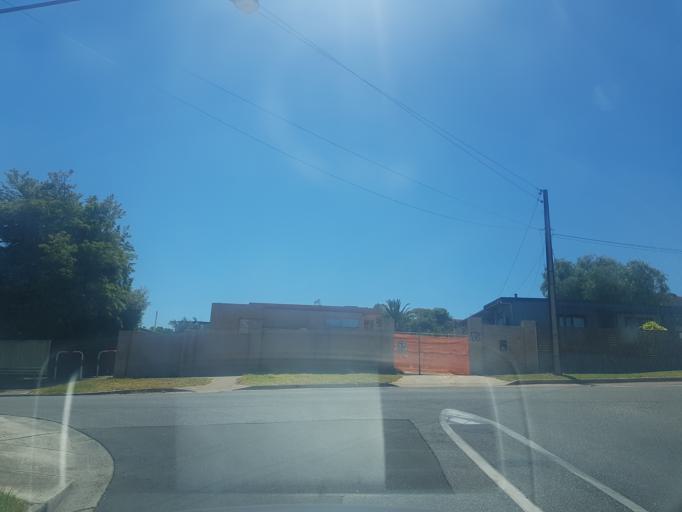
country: AU
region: South Australia
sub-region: Salisbury
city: Ingle Farm
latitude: -34.8151
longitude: 138.6533
